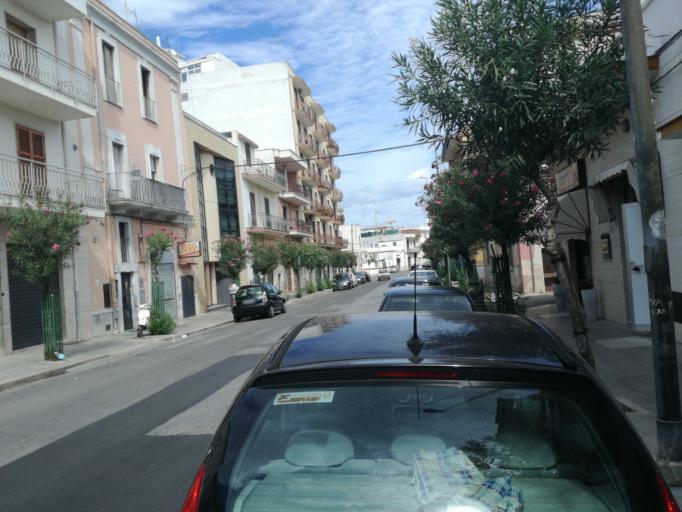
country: IT
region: Apulia
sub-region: Provincia di Bari
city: Triggiano
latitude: 41.0628
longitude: 16.9274
